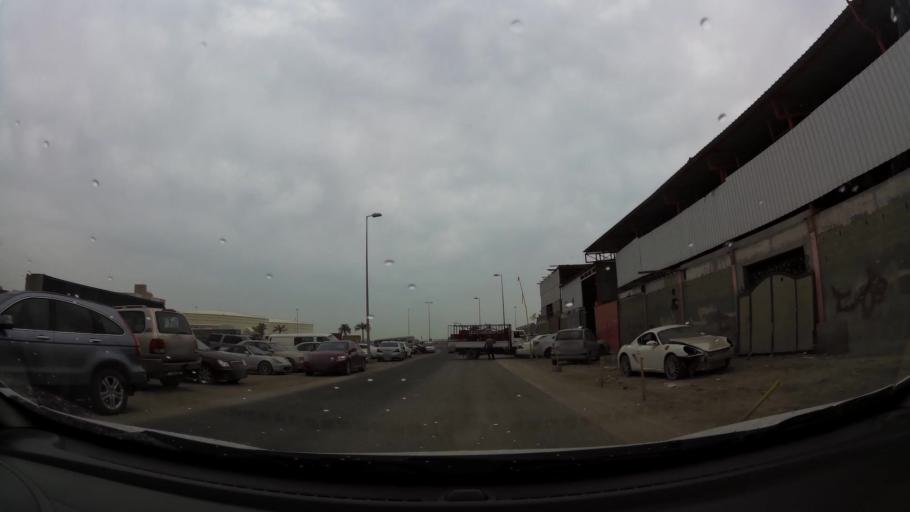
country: BH
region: Northern
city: Madinat `Isa
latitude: 26.1828
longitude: 50.5226
